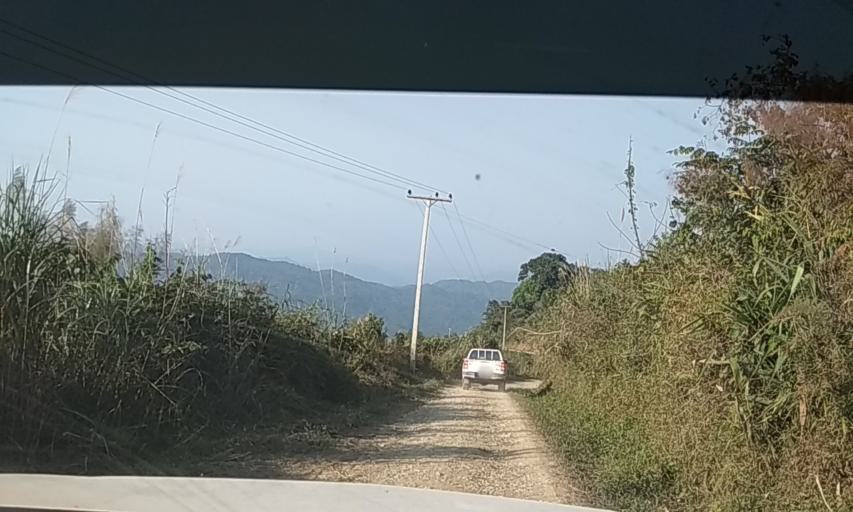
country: LA
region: Phongsali
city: Phongsali
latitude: 21.6642
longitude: 102.1795
